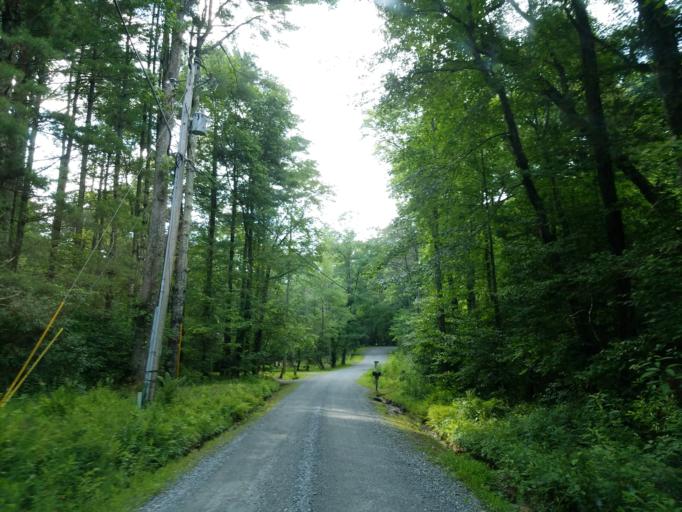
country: US
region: Georgia
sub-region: Gilmer County
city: Ellijay
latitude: 34.6468
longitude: -84.2878
